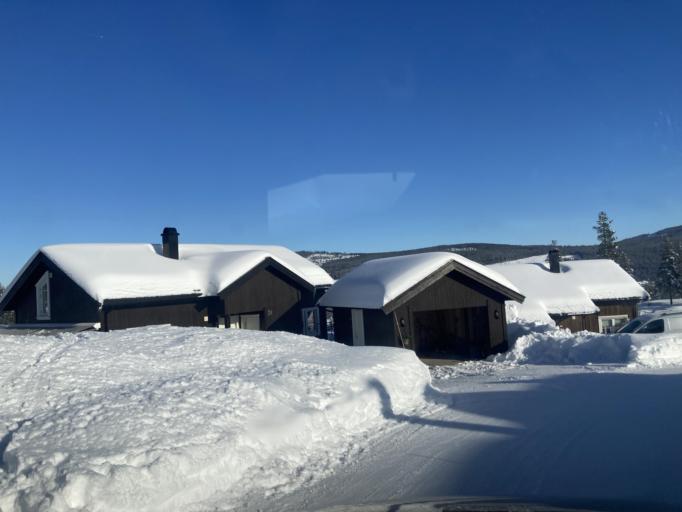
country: NO
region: Hedmark
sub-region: Trysil
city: Innbygda
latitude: 61.2989
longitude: 12.2406
